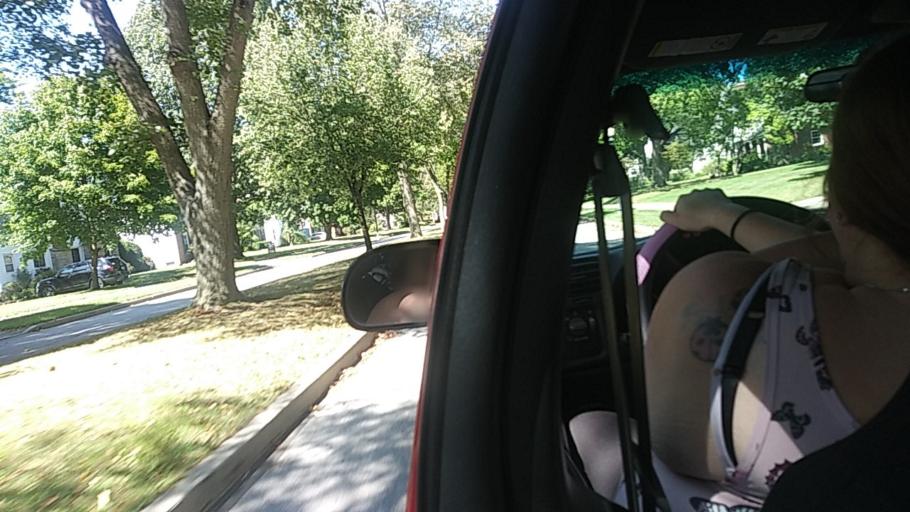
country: US
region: Ohio
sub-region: Summit County
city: Fairlawn
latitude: 41.1119
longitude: -81.5614
